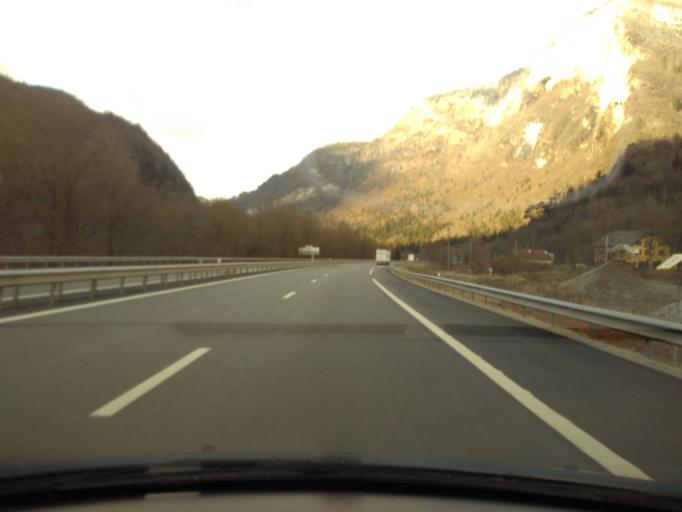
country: FR
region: Rhone-Alpes
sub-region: Departement de la Haute-Savoie
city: Magland
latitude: 46.0376
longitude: 6.6090
